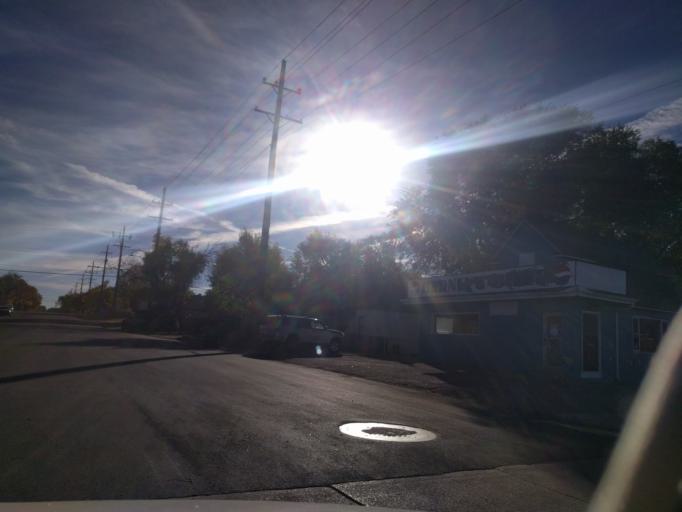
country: US
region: Colorado
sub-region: El Paso County
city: Colorado Springs
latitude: 38.8233
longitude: -104.8295
